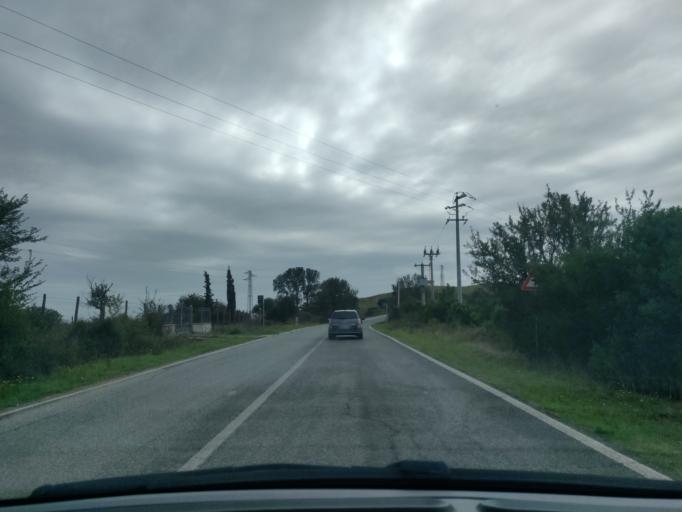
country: IT
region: Latium
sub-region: Citta metropolitana di Roma Capitale
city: Allumiere
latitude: 42.1184
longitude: 11.8616
